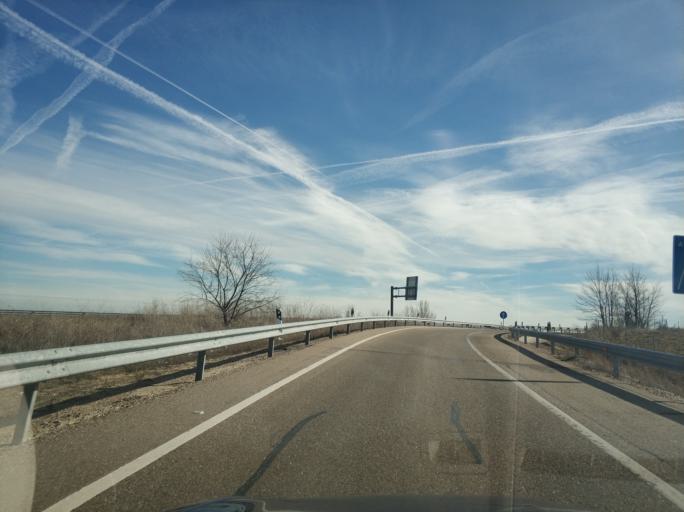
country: ES
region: Castille and Leon
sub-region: Provincia de Zamora
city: Cazurra
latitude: 41.4152
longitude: -5.7223
